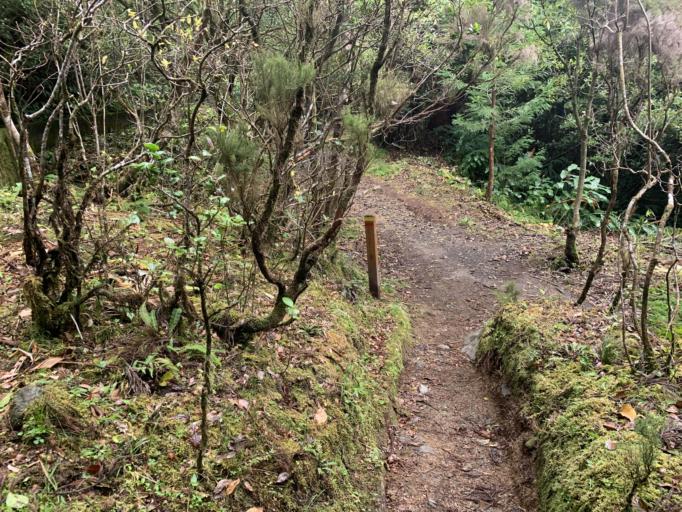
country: PT
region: Azores
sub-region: Vila Franca do Campo
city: Vila Franca do Campo
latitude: 37.7458
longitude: -25.4758
